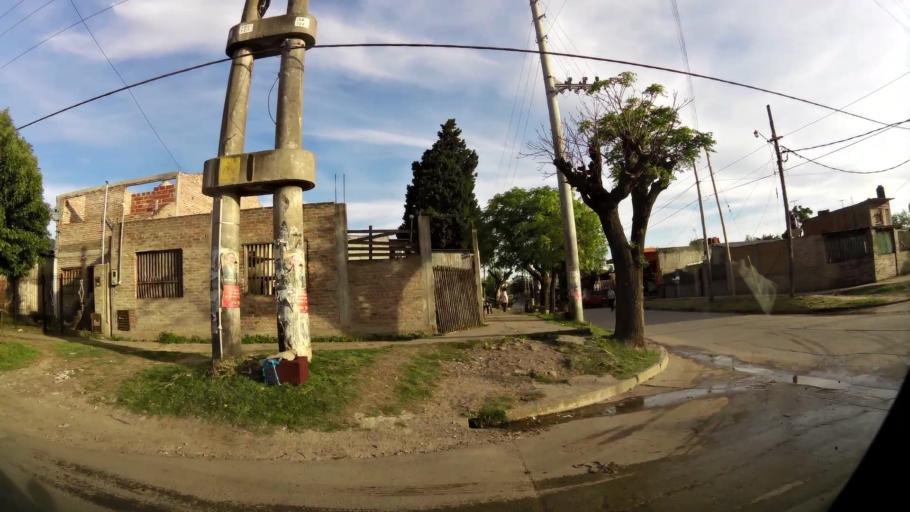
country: AR
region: Buenos Aires
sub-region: Partido de Almirante Brown
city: Adrogue
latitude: -34.7849
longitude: -58.3328
